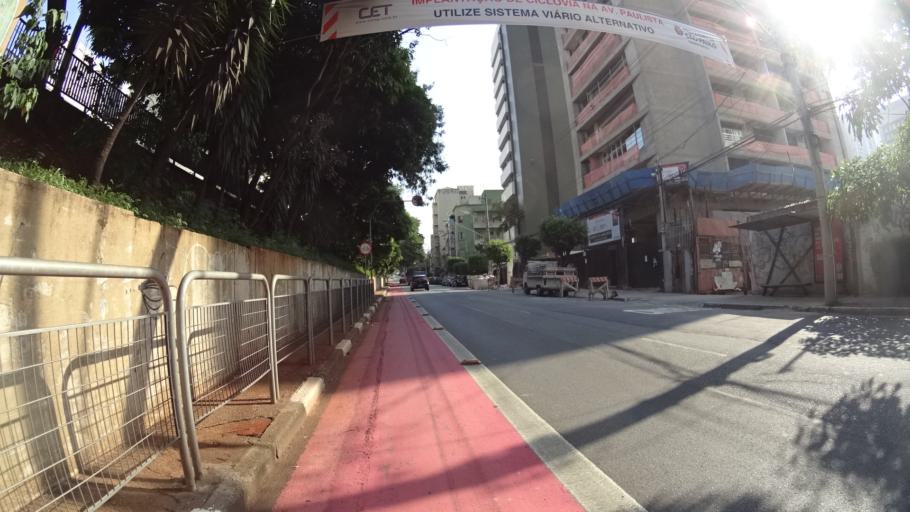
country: BR
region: Sao Paulo
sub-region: Sao Paulo
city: Sao Paulo
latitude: -23.5649
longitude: -46.6416
